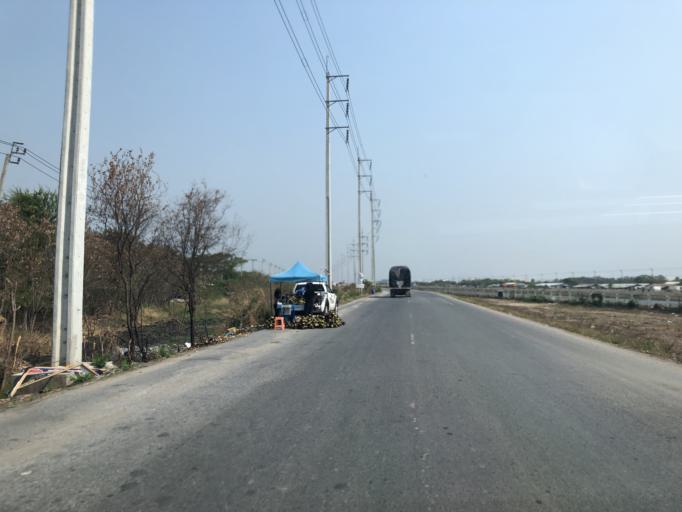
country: TH
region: Samut Prakan
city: Bang Bo District
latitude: 13.5080
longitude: 100.7443
